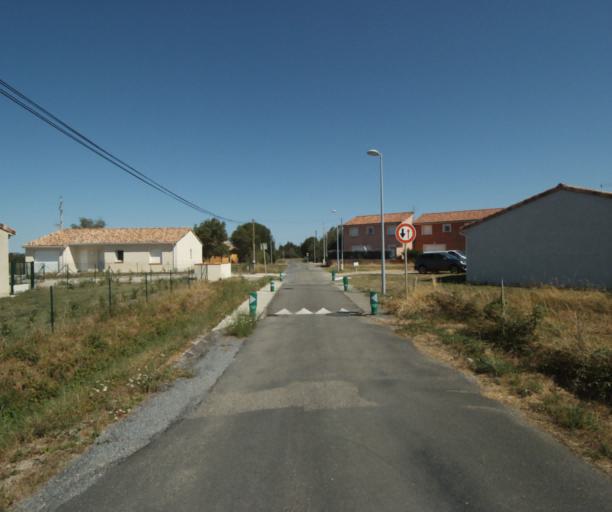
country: FR
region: Midi-Pyrenees
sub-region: Departement de la Haute-Garonne
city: Revel
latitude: 43.4677
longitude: 1.9984
